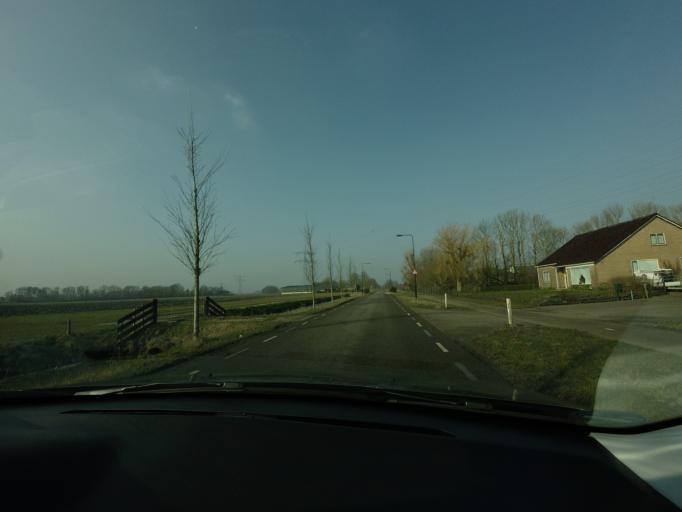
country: NL
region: North Holland
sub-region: Gemeente Heerhugowaard
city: Heerhugowaard
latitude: 52.6374
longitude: 4.8711
